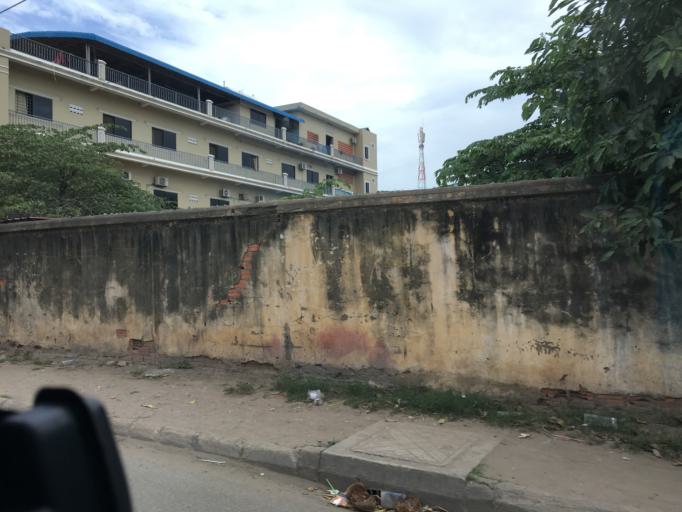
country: KH
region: Phnom Penh
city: Phnom Penh
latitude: 11.5313
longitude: 104.9305
